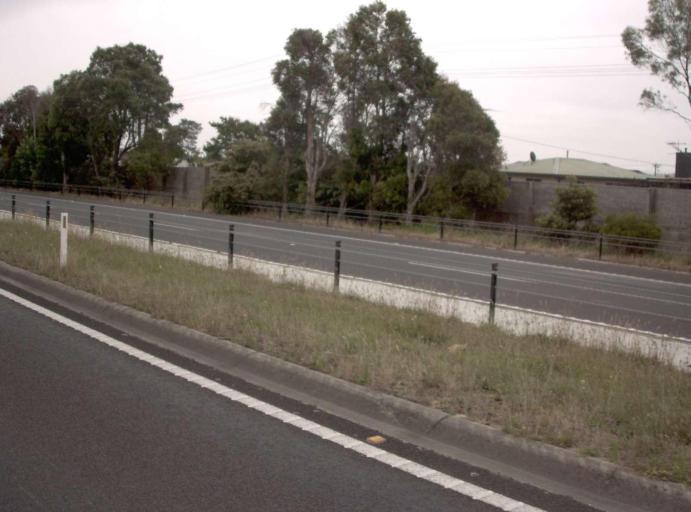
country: AU
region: Victoria
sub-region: Latrobe
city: Moe
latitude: -38.1858
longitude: 146.2489
